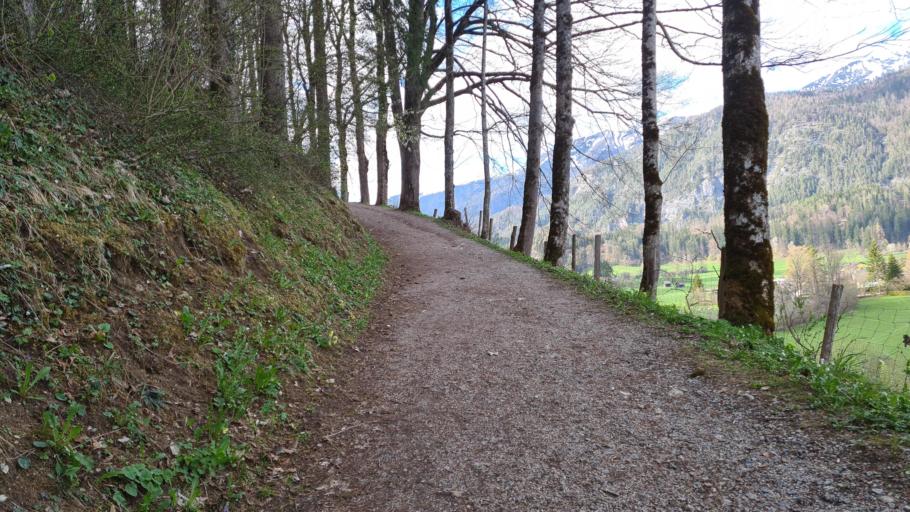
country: AT
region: Upper Austria
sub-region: Politischer Bezirk Kirchdorf an der Krems
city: Rossleithen
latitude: 47.7270
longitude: 14.3241
